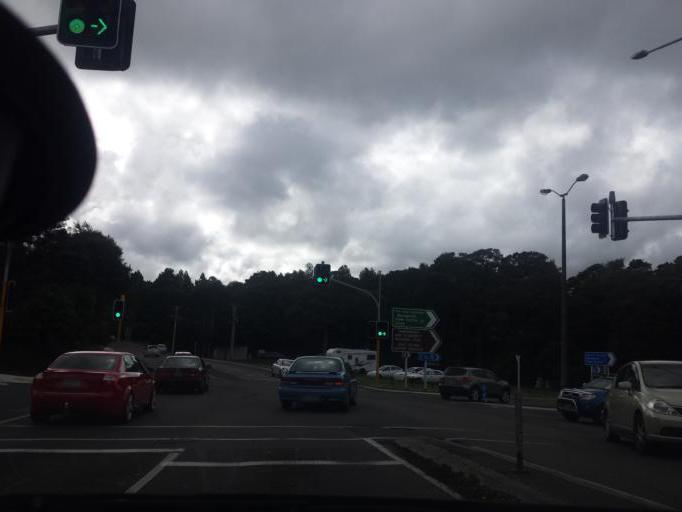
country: NZ
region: Auckland
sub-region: Auckland
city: Warkworth
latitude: -36.3971
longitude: 174.6607
